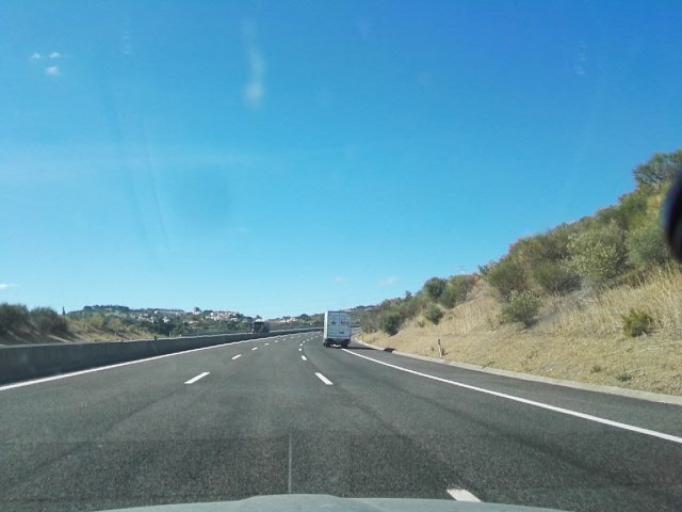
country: PT
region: Lisbon
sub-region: Vila Franca de Xira
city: Castanheira do Ribatejo
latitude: 38.9991
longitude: -9.0162
